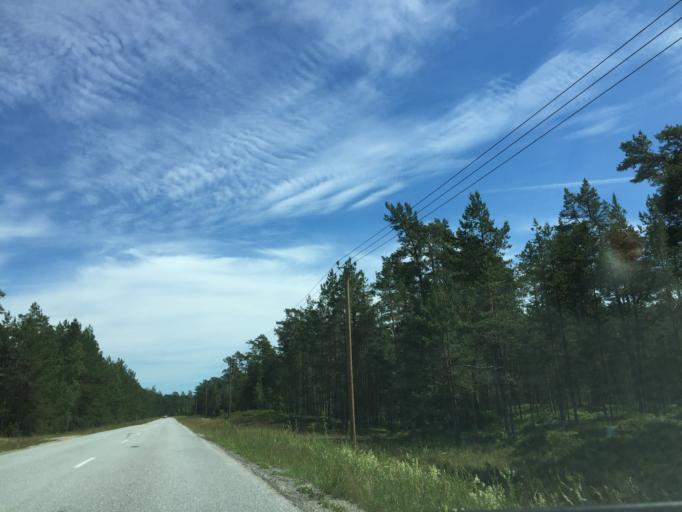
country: LV
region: Rojas
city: Roja
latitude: 57.5721
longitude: 22.6387
